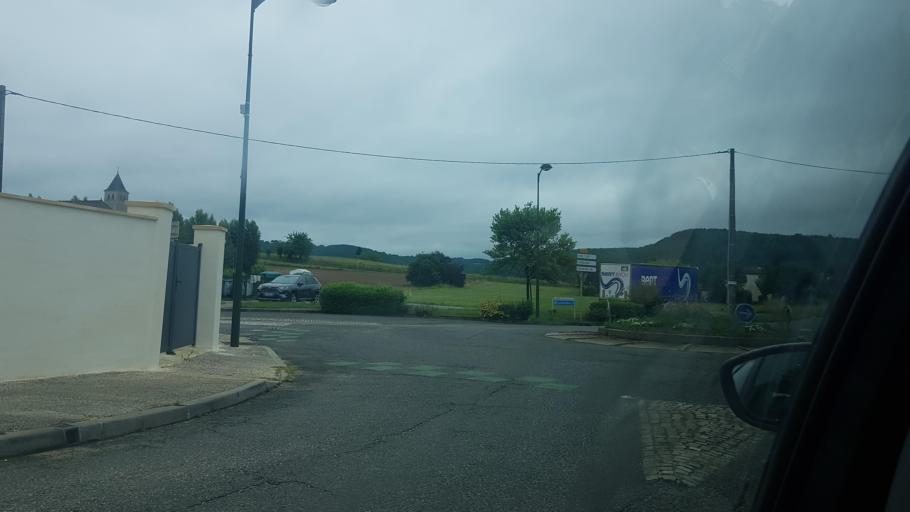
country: FR
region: Aquitaine
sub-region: Departement du Lot-et-Garonne
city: Montayral
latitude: 44.4927
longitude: 1.0828
